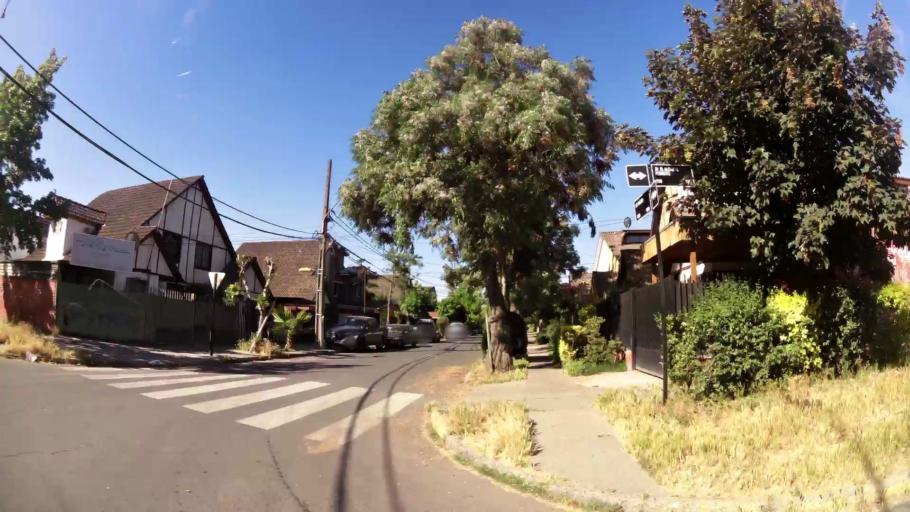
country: CL
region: Santiago Metropolitan
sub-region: Provincia de Maipo
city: San Bernardo
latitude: -33.5623
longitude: -70.7884
